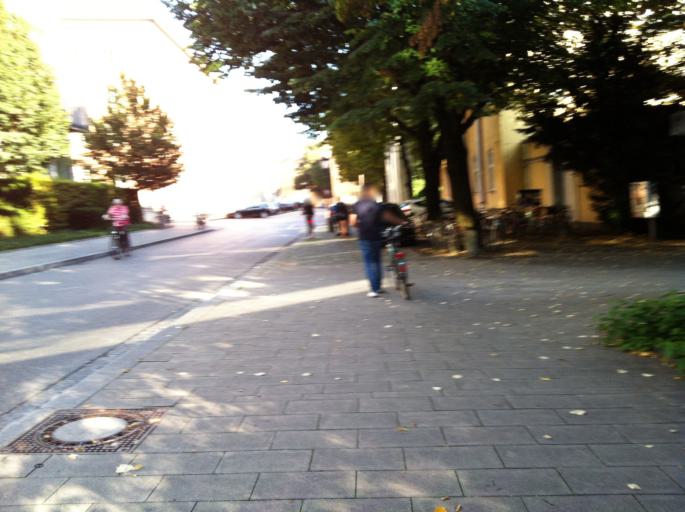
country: DE
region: Bavaria
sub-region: Upper Bavaria
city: Munich
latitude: 48.1427
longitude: 11.5642
